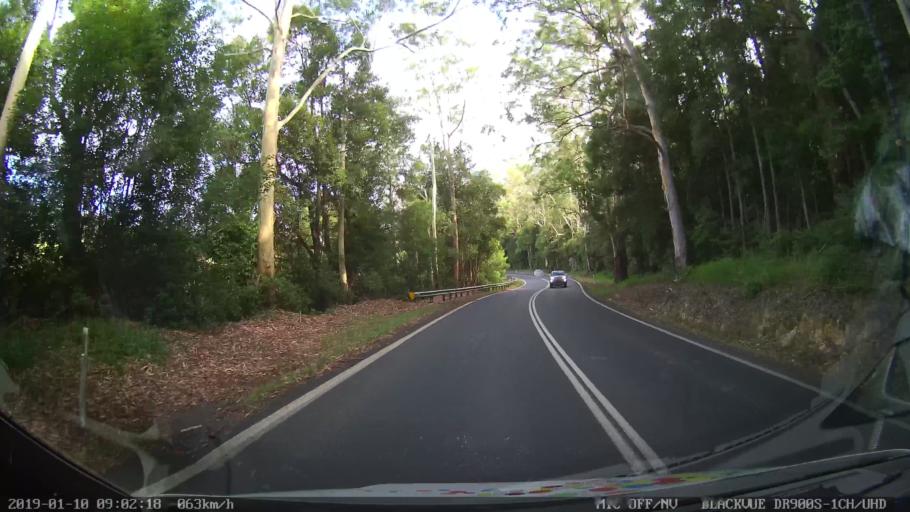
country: AU
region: New South Wales
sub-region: Coffs Harbour
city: Coffs Harbour
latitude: -30.2737
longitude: 153.0533
